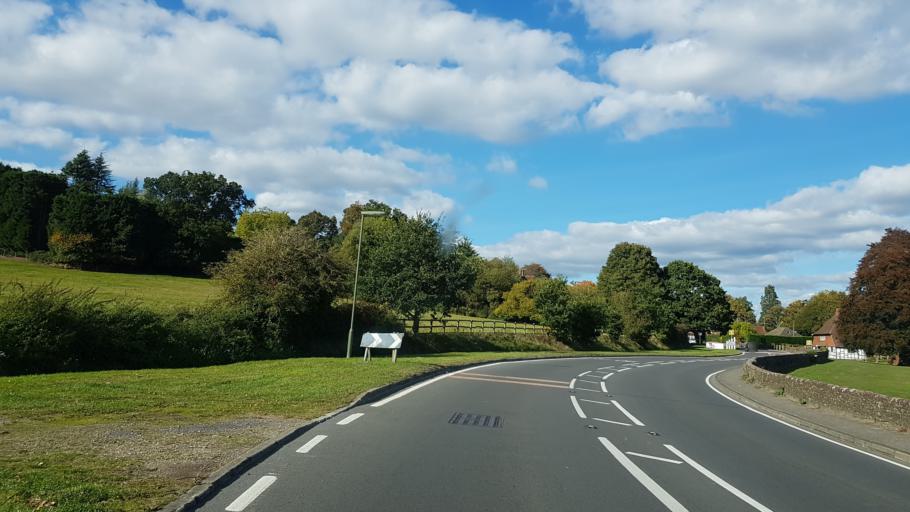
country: GB
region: England
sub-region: Surrey
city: Milford
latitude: 51.1451
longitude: -0.6467
